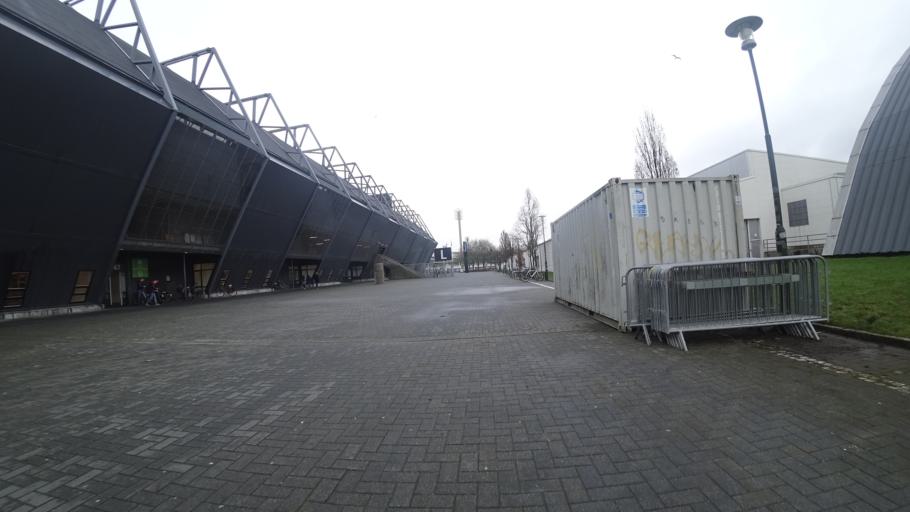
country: SE
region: Skane
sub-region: Malmo
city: Malmoe
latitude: 55.5831
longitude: 12.9889
